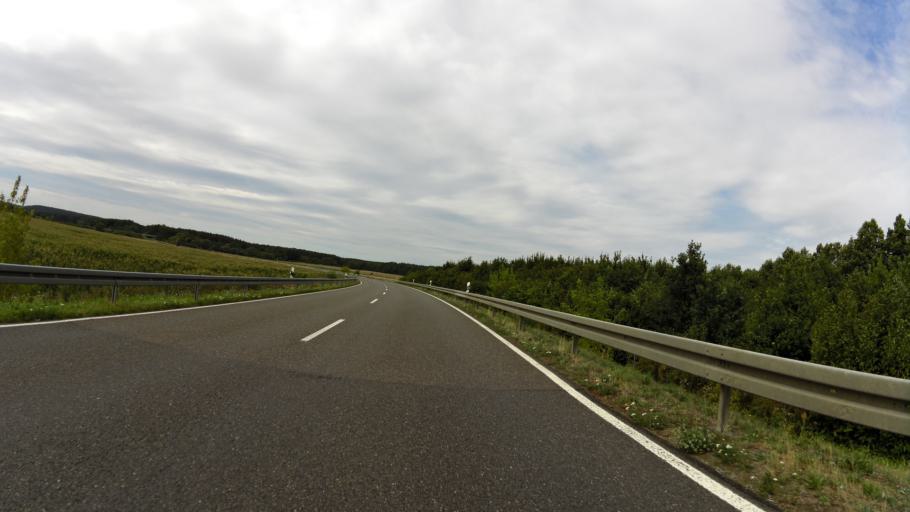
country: DE
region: Brandenburg
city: Schenkendobern
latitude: 51.8949
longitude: 14.6510
